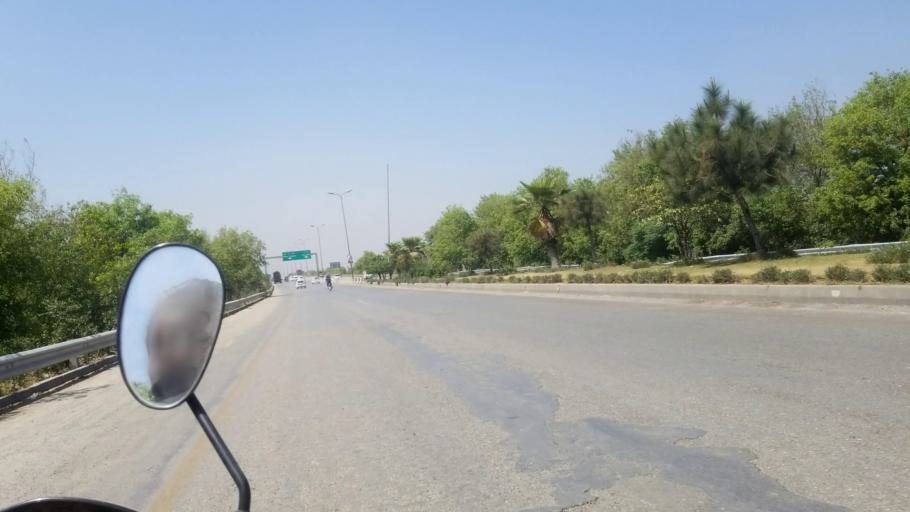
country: PK
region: Khyber Pakhtunkhwa
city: Peshawar
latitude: 34.0253
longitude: 71.6339
